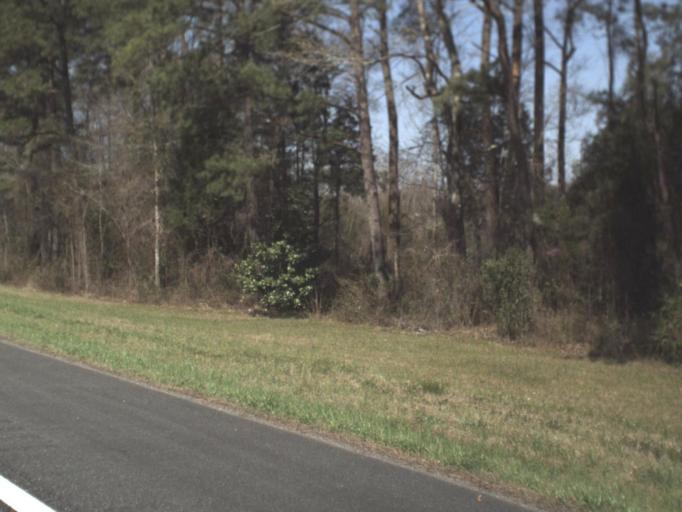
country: US
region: Florida
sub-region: Jackson County
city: Marianna
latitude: 30.7558
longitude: -85.3568
